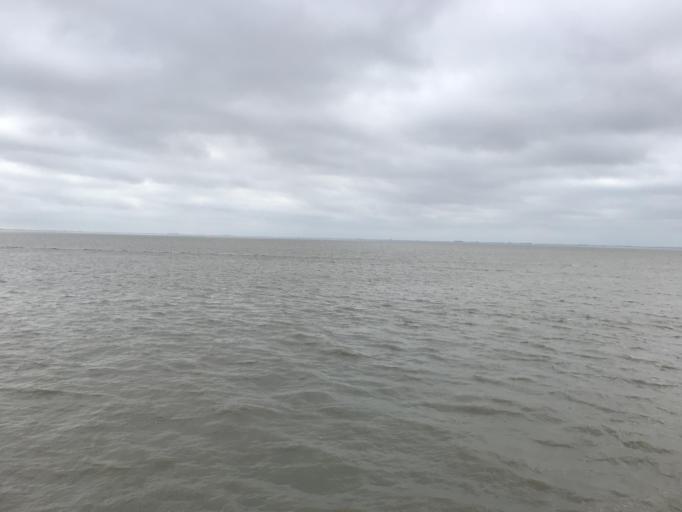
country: DE
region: Lower Saxony
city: Emden
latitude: 53.3307
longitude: 7.1267
